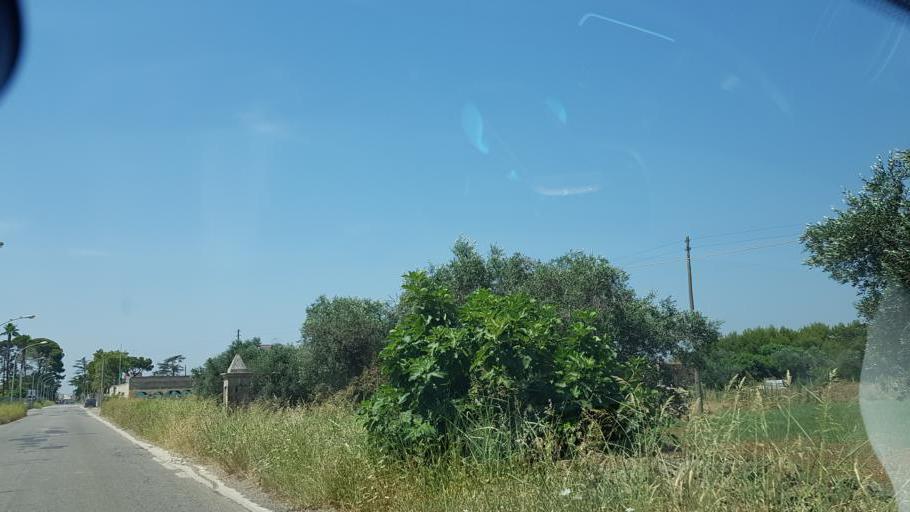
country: IT
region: Apulia
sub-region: Provincia di Brindisi
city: Mesagne
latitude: 40.5486
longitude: 17.8183
